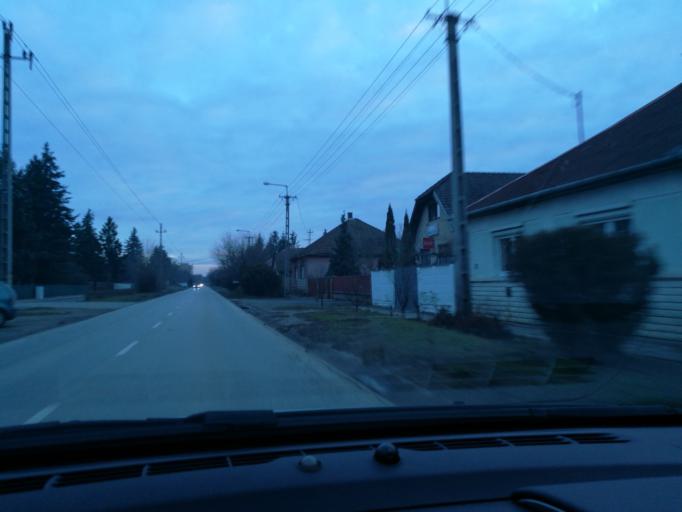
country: HU
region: Szabolcs-Szatmar-Bereg
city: Nyiregyhaza
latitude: 47.9748
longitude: 21.7065
